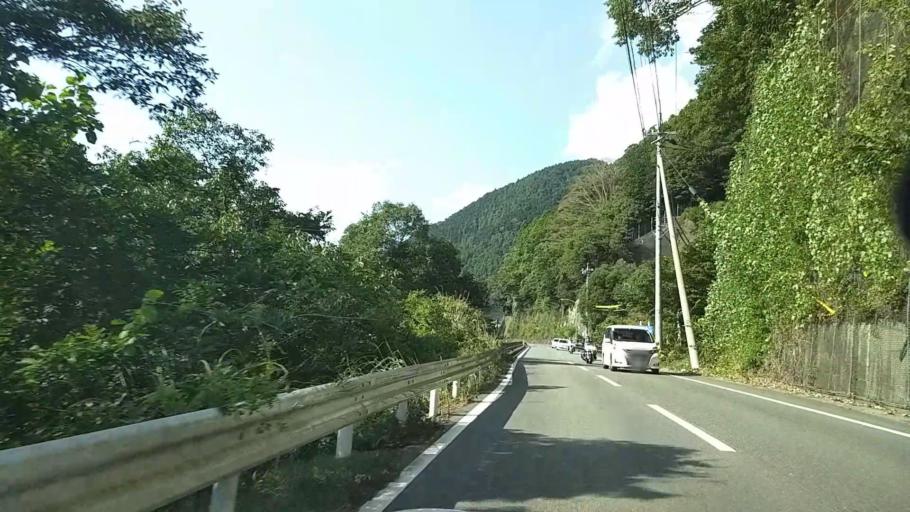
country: JP
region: Shizuoka
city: Fujinomiya
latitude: 35.2874
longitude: 138.4601
